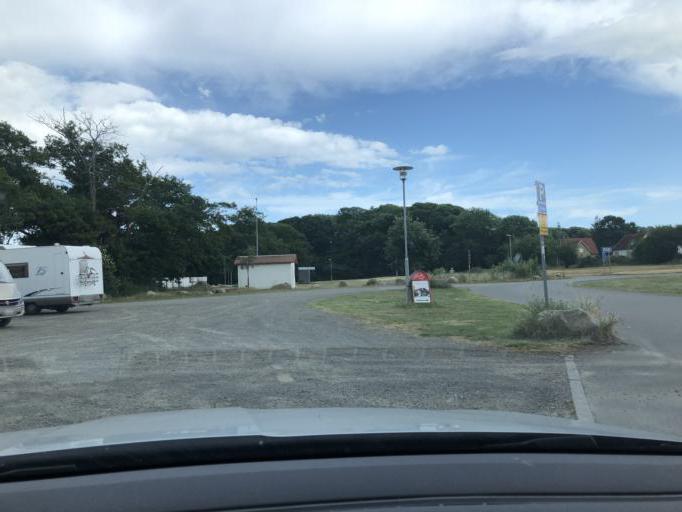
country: SE
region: Skane
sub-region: Simrishamns Kommun
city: Kivik
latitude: 55.6862
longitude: 14.2306
